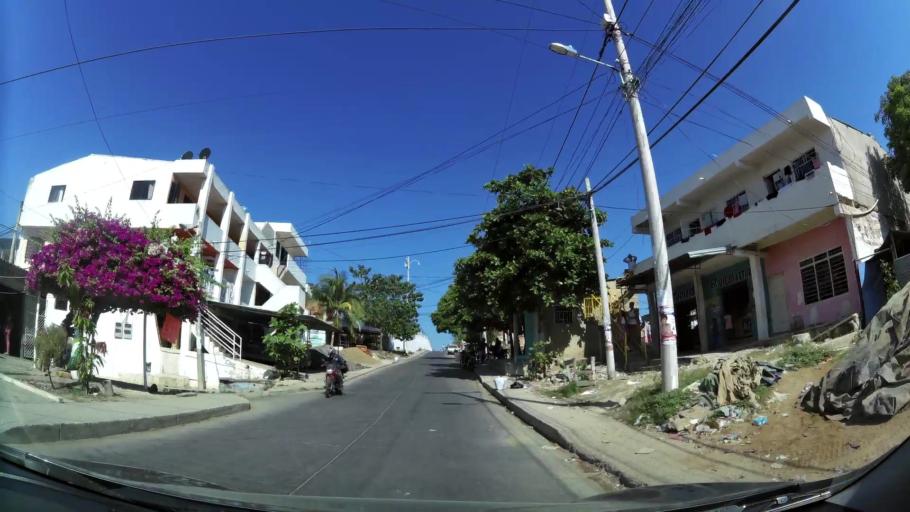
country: CO
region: Bolivar
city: Cartagena
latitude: 10.3957
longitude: -75.5094
